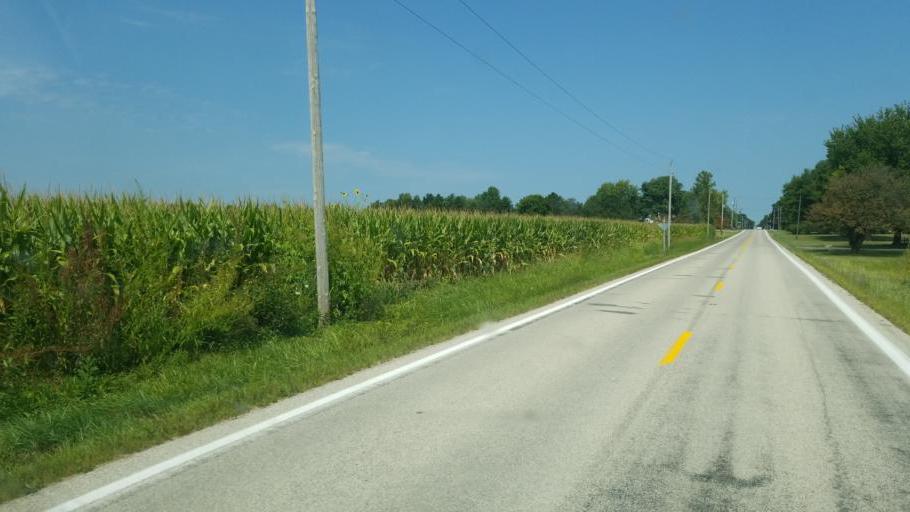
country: US
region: Ohio
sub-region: Marion County
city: Marion
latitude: 40.6053
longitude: -83.2174
